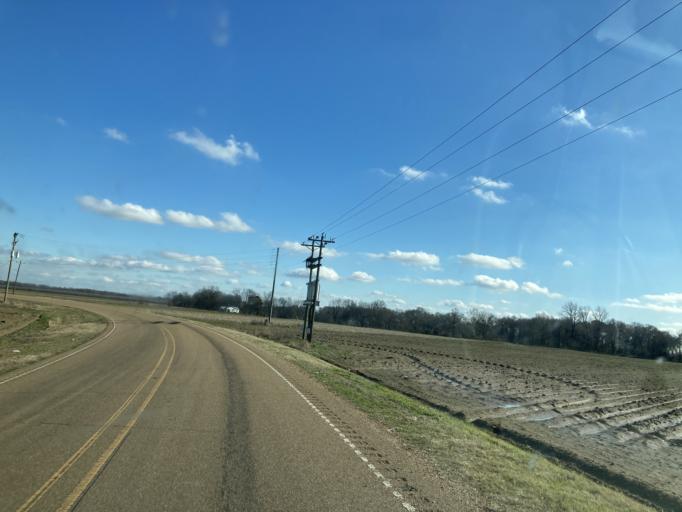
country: US
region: Mississippi
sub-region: Yazoo County
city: Yazoo City
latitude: 32.9622
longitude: -90.4936
